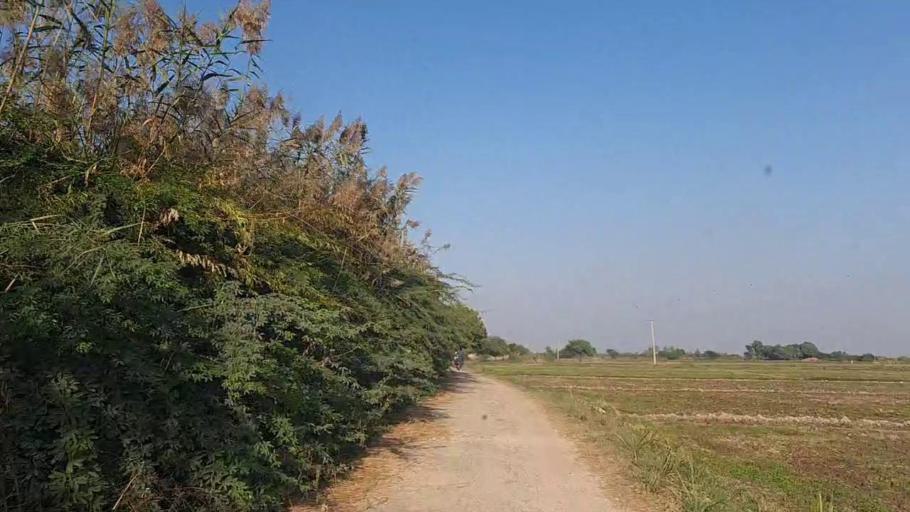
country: PK
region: Sindh
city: Thatta
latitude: 24.7202
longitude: 67.9443
